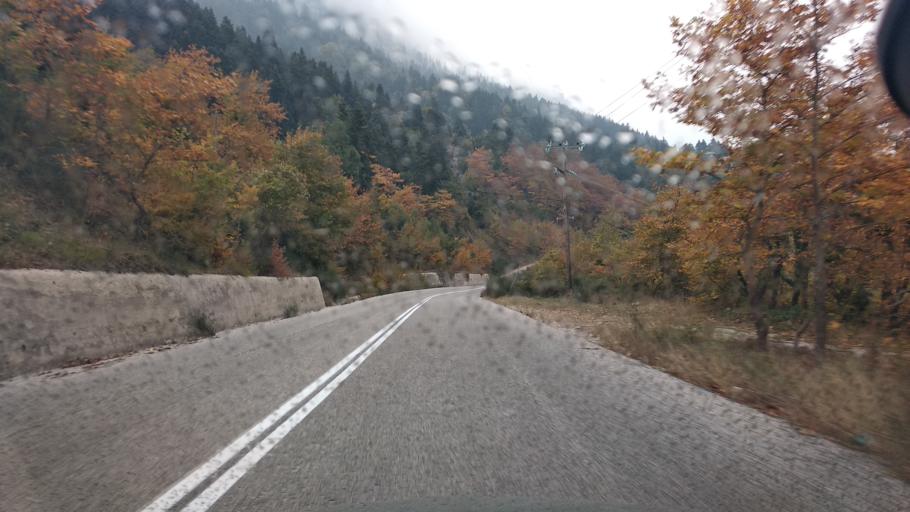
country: GR
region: Thessaly
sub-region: Trikala
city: Pyli
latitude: 39.4921
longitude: 21.5437
